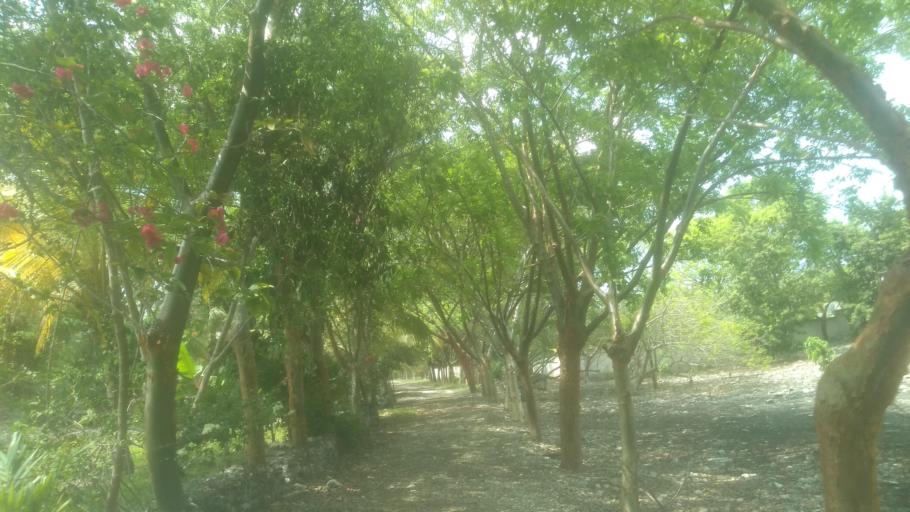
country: MX
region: Veracruz
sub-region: Emiliano Zapata
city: Plan del Rio
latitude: 19.3888
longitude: -96.6341
